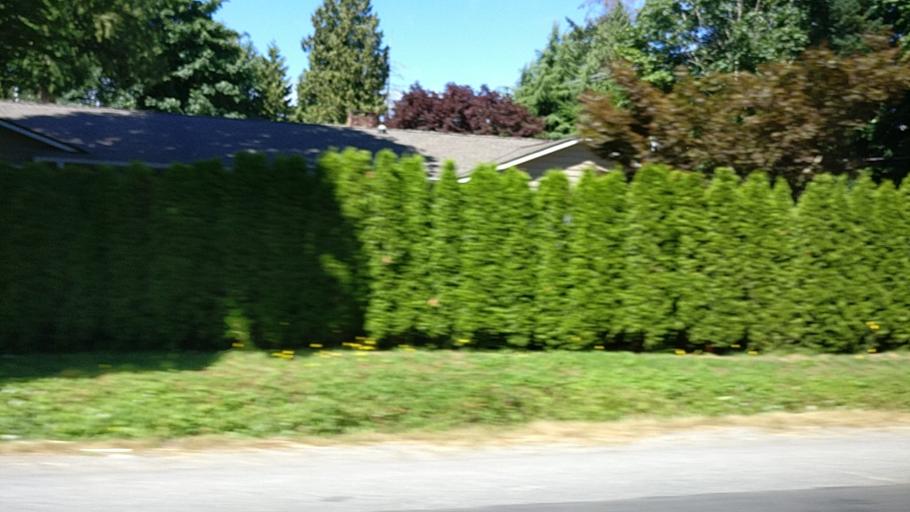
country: CA
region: British Columbia
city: Surrey
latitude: 49.0567
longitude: -122.8564
